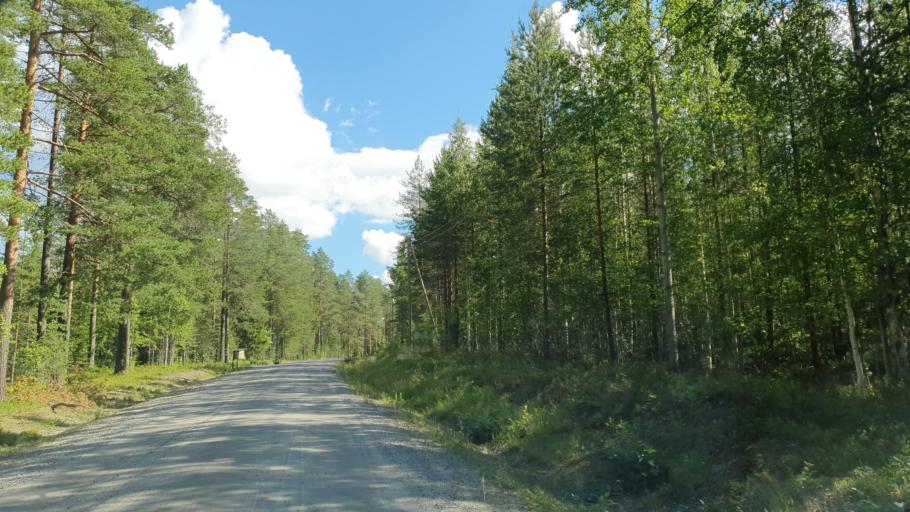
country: FI
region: Kainuu
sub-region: Kehys-Kainuu
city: Kuhmo
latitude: 64.1054
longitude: 29.3969
